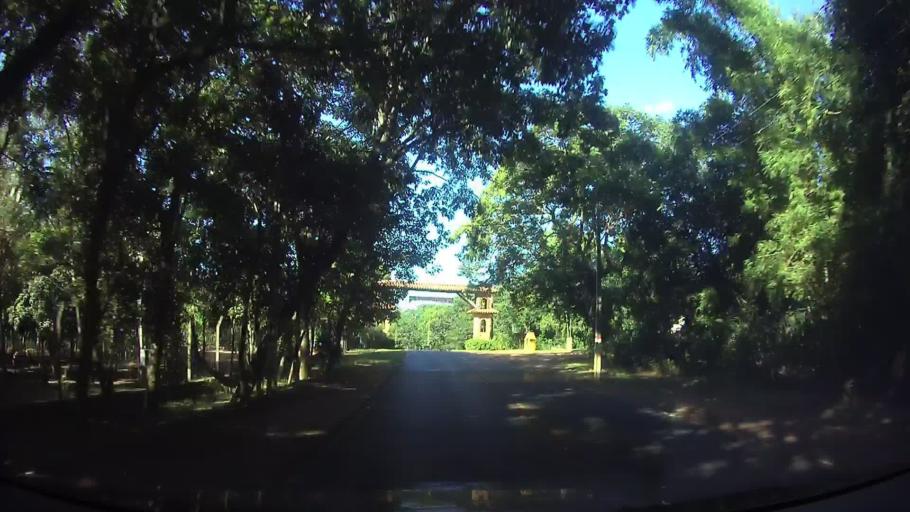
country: PY
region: Cordillera
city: Atyra
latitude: -25.2889
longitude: -57.1796
